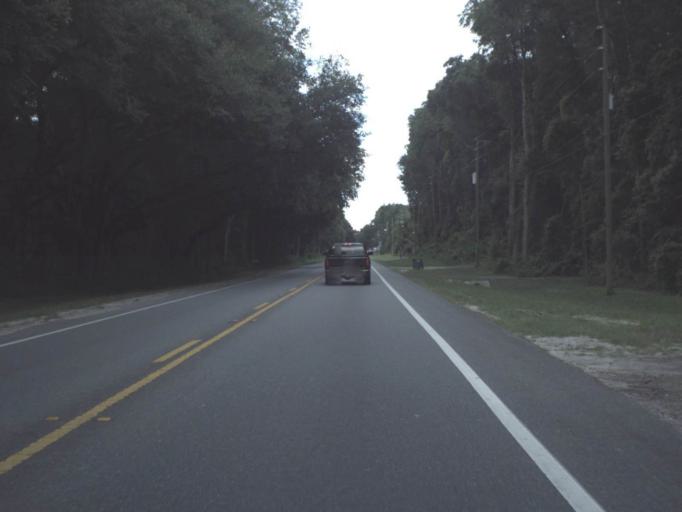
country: US
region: Florida
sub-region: Alachua County
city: Newberry
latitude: 29.6460
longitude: -82.6288
